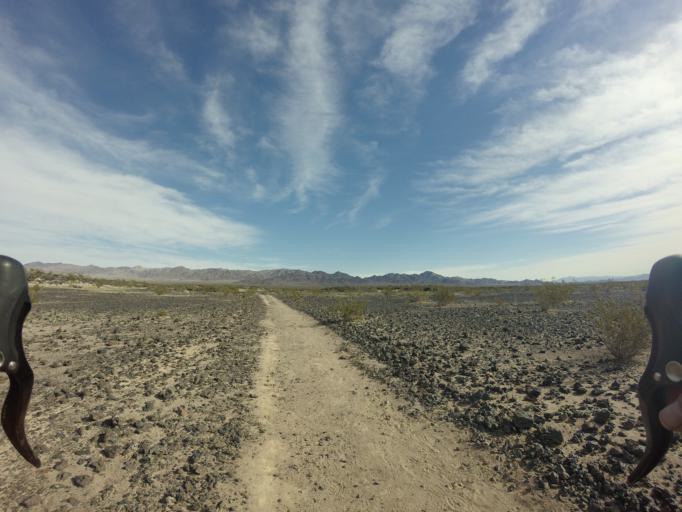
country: US
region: California
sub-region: San Bernardino County
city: Twentynine Palms
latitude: 34.5552
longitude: -115.7839
